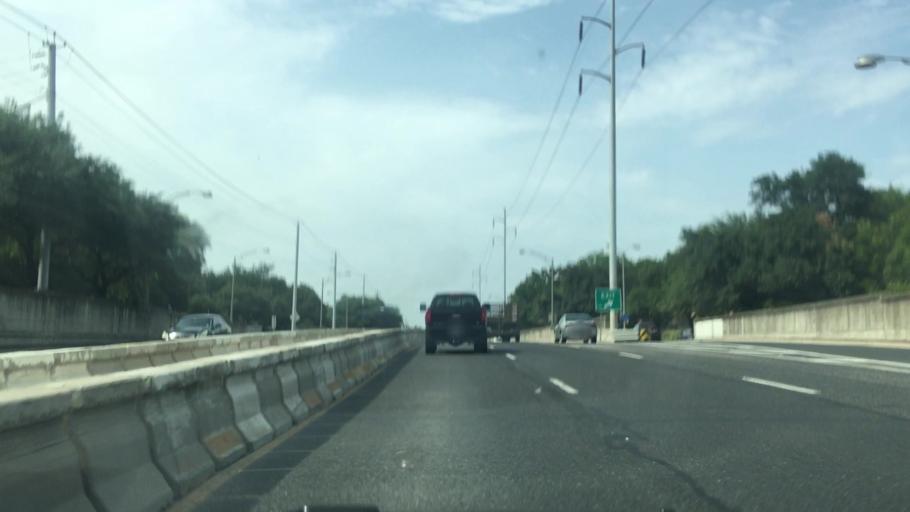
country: US
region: Texas
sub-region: Dallas County
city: University Park
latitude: 32.8344
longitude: -96.8145
